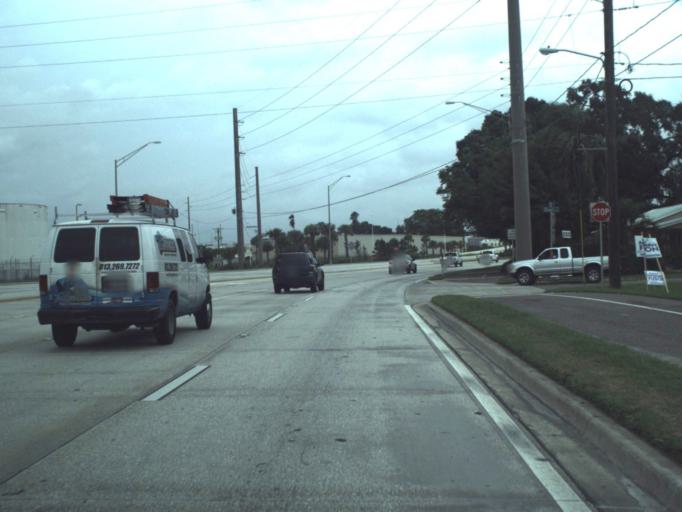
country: US
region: Florida
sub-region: Hillsborough County
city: Tampa
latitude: 27.9469
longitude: -82.4364
